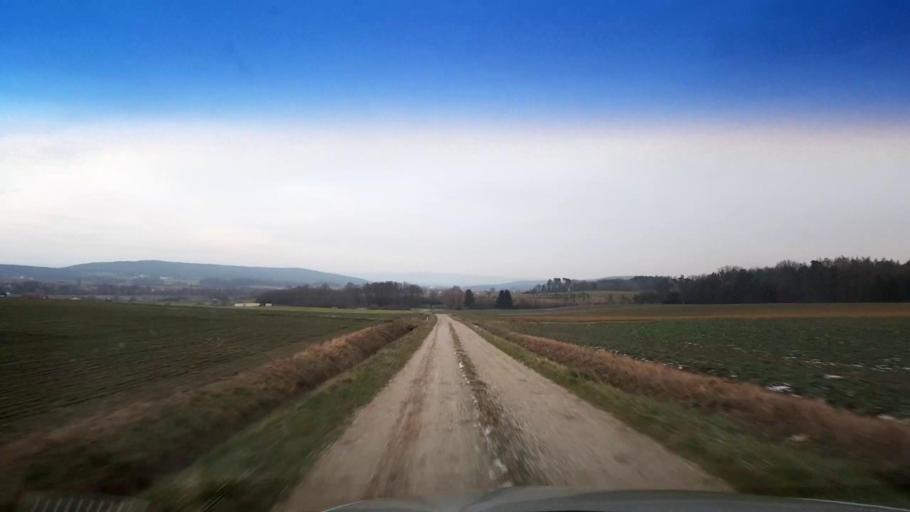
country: DE
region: Bavaria
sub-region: Upper Franconia
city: Frensdorf
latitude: 49.8140
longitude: 10.8277
